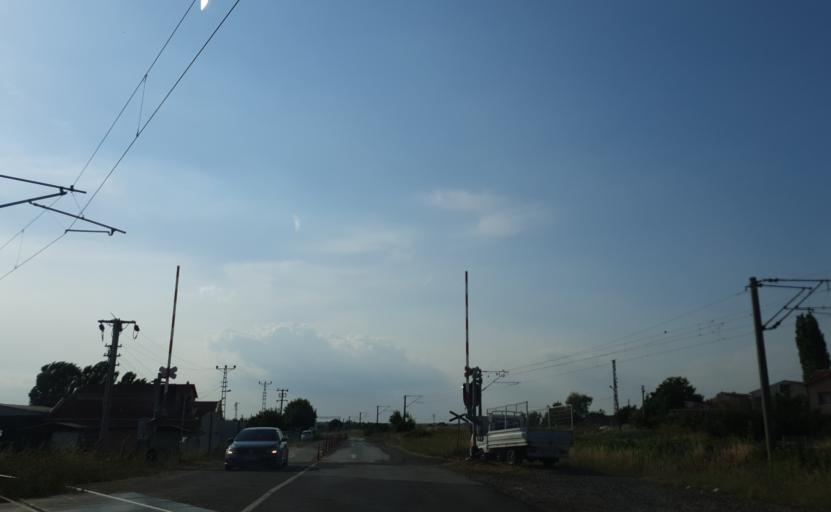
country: TR
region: Tekirdag
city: Muratli
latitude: 41.1781
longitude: 27.4889
